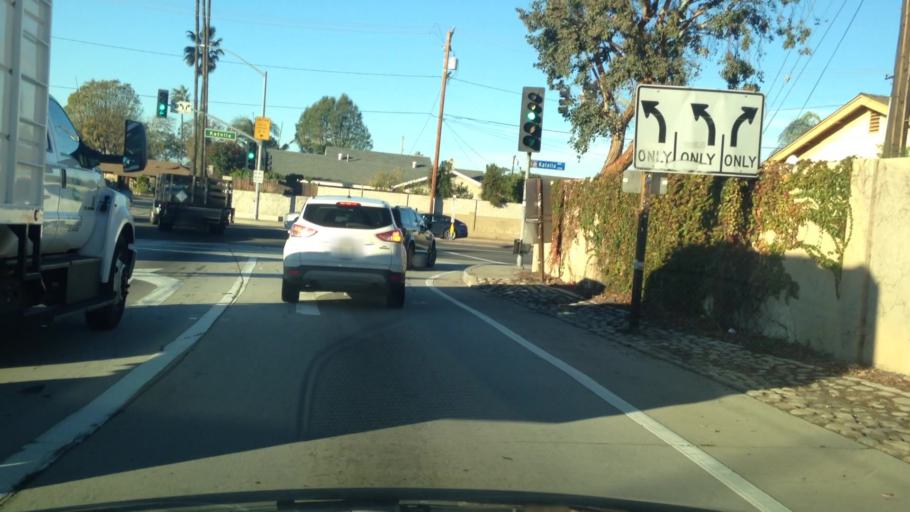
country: US
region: California
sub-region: Orange County
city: Villa Park
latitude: 33.8099
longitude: -117.8306
